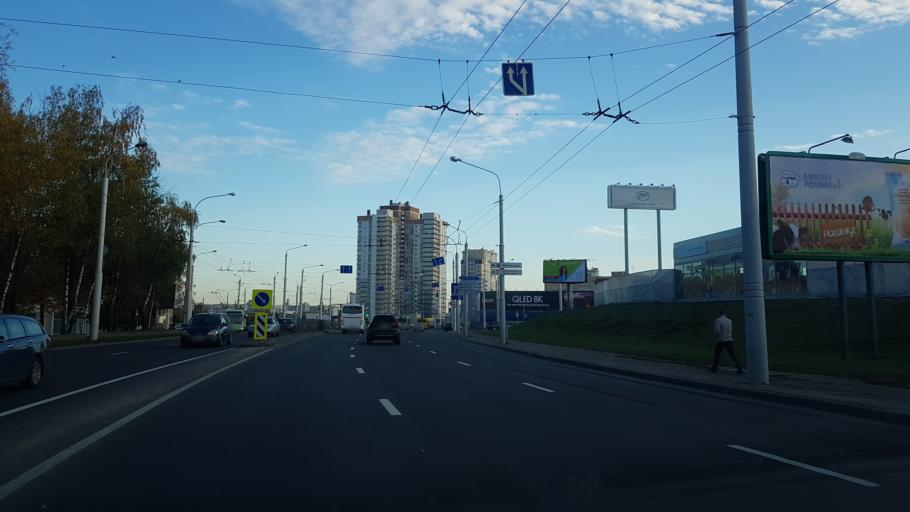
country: BY
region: Minsk
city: Minsk
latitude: 53.8870
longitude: 27.5656
